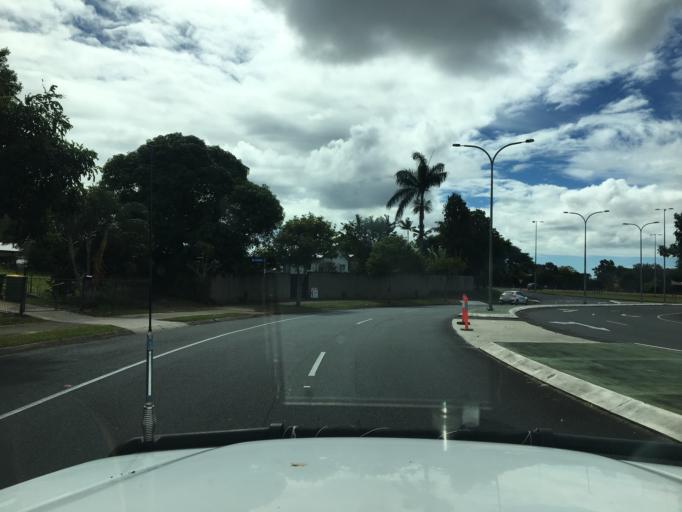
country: AU
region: Queensland
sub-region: Cairns
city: Woree
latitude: -16.9884
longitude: 145.7395
